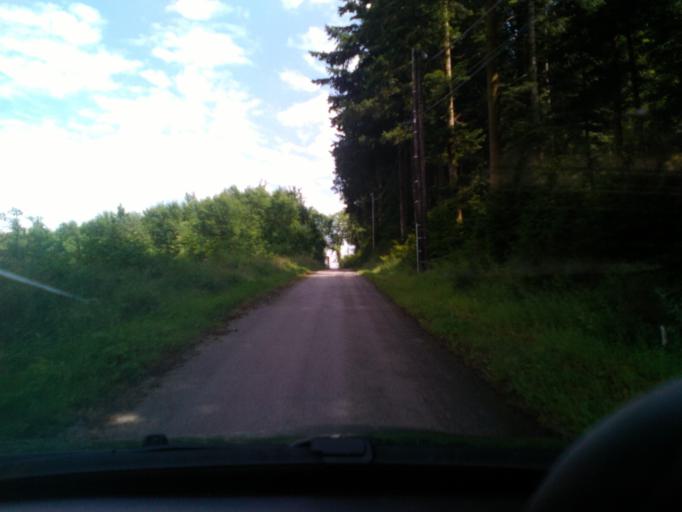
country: FR
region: Lorraine
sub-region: Departement des Vosges
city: Senones
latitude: 48.3360
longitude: 7.0020
